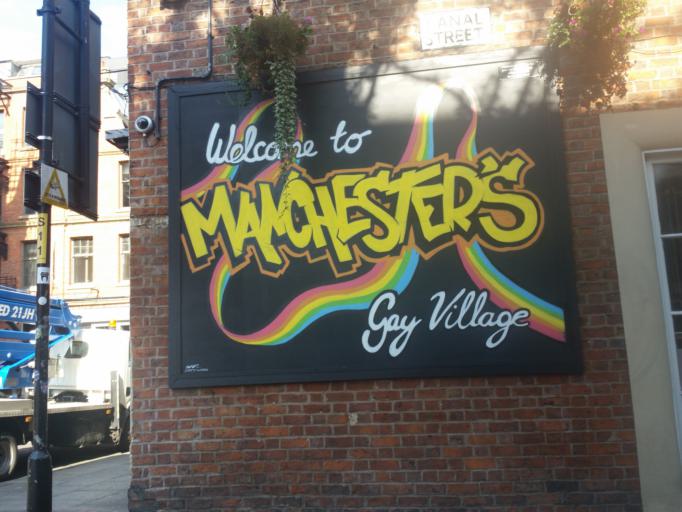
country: GB
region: England
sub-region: Manchester
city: Manchester
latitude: 53.4776
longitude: -2.2359
